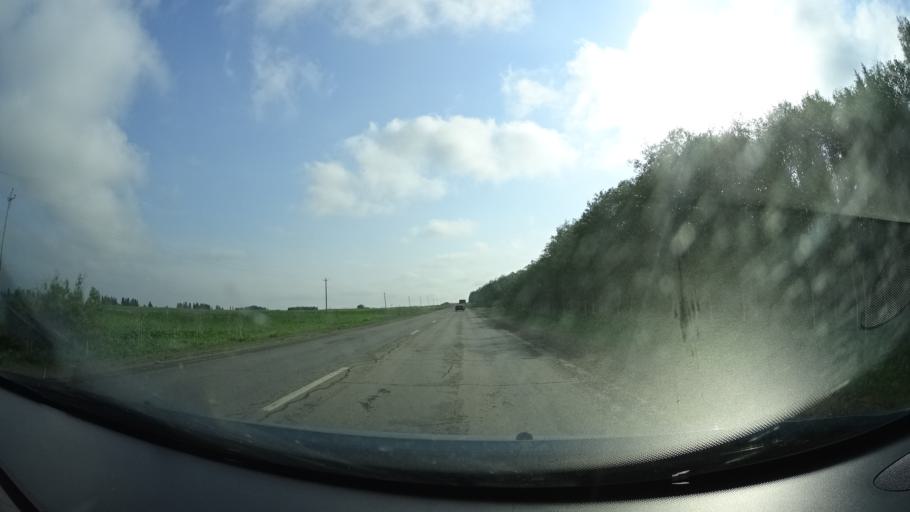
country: RU
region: Perm
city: Kultayevo
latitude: 57.8556
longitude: 55.8577
